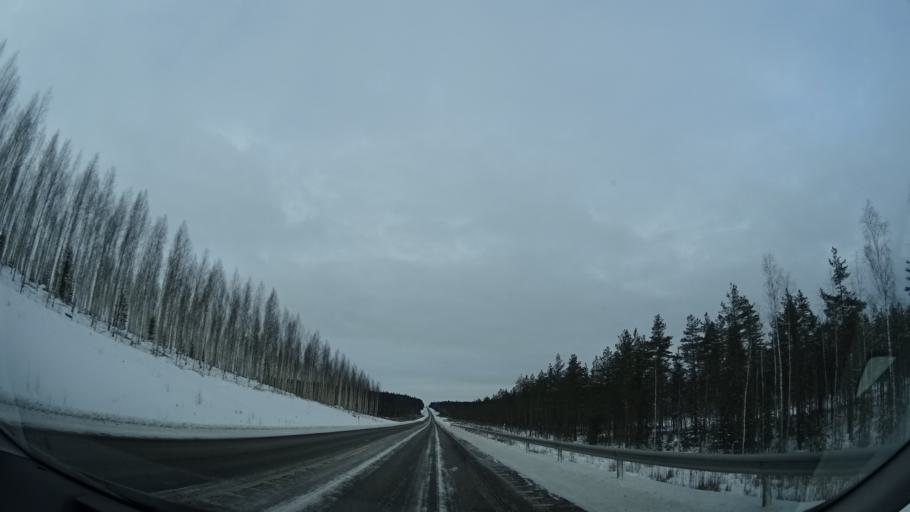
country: FI
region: Uusimaa
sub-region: Helsinki
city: Kaerkoelae
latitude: 60.6210
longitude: 23.9980
